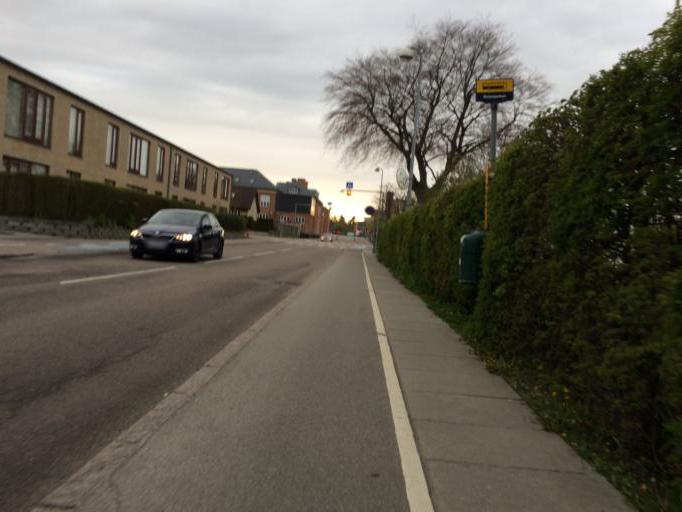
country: DK
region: Capital Region
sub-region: Hoje-Taastrup Kommune
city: Taastrup
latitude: 55.6454
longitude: 12.3016
